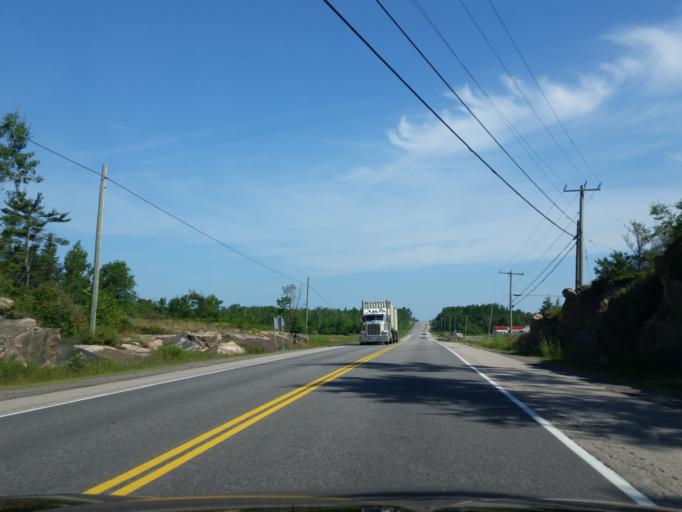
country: CA
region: Ontario
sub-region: Parry Sound District
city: Parry Sound
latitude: 45.8059
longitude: -80.5393
